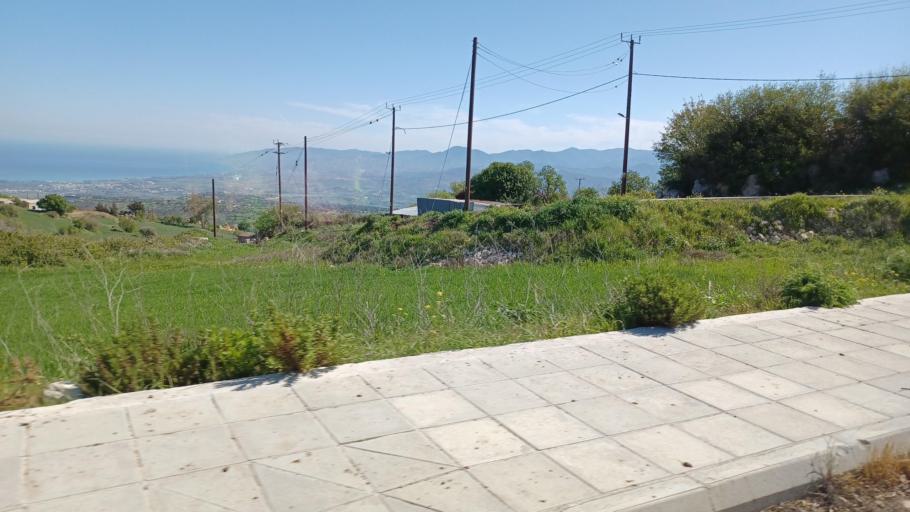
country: CY
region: Pafos
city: Polis
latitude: 34.9645
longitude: 32.3896
